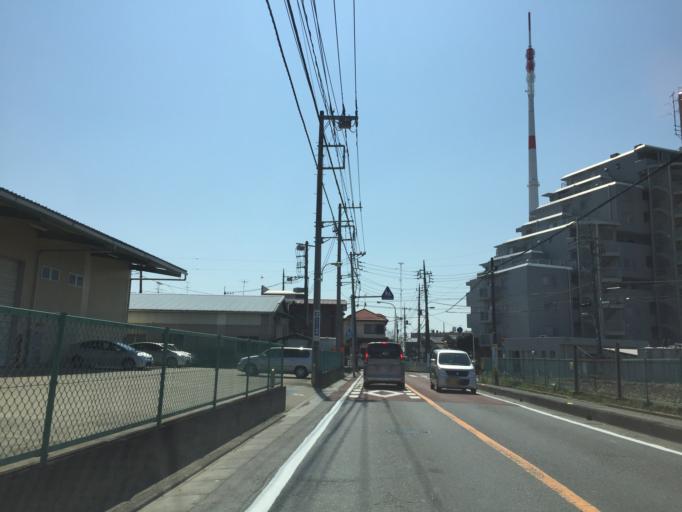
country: JP
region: Saitama
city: Yono
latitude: 35.8553
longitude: 139.6153
